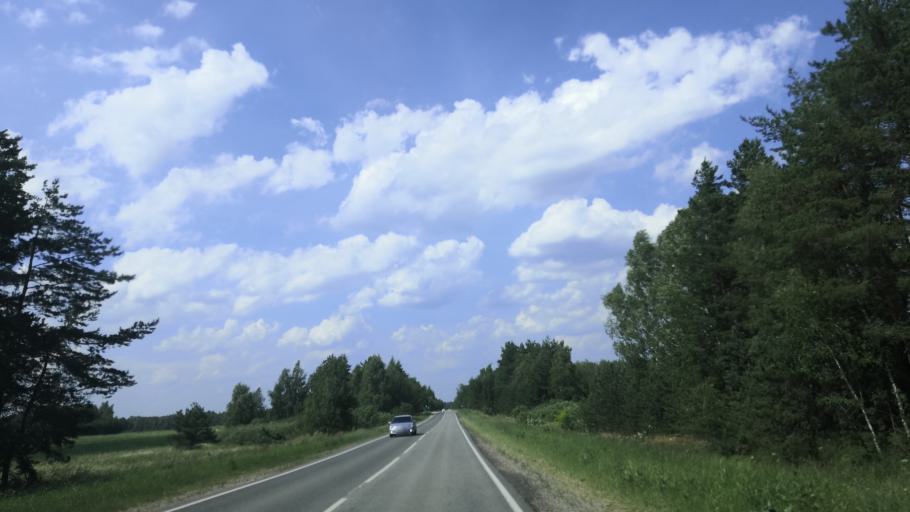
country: RU
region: Rjazan
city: Murmino
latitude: 54.5747
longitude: 40.1117
